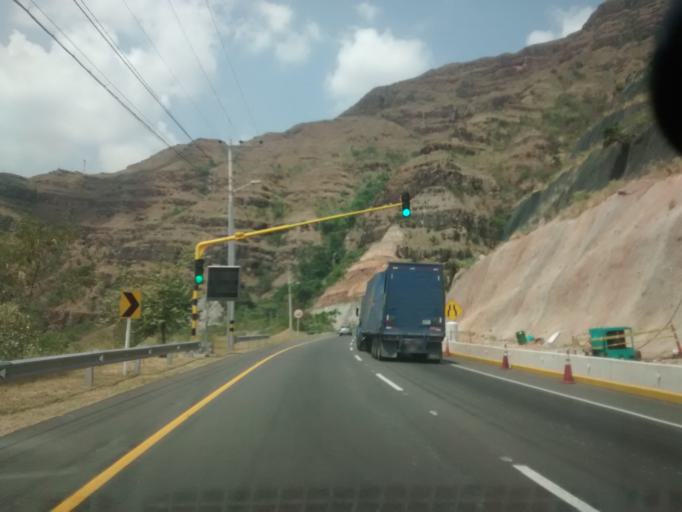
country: CO
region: Tolima
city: Valle de San Juan
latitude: 4.2843
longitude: -75.0213
